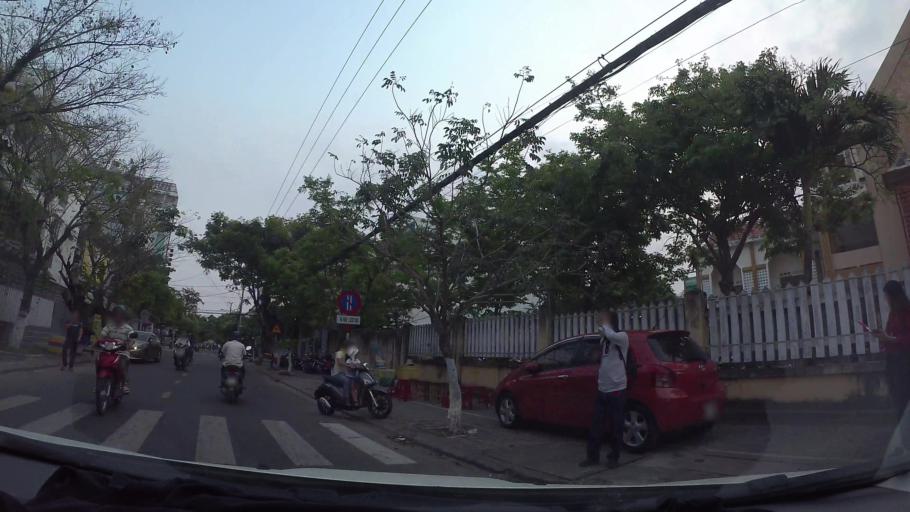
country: VN
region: Da Nang
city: Son Tra
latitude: 16.0481
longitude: 108.2412
